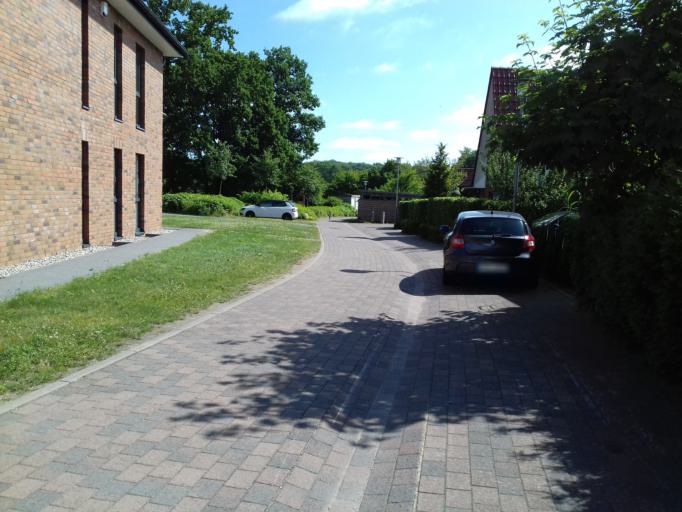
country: DE
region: Schleswig-Holstein
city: Neumunster
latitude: 54.0780
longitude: 10.0055
